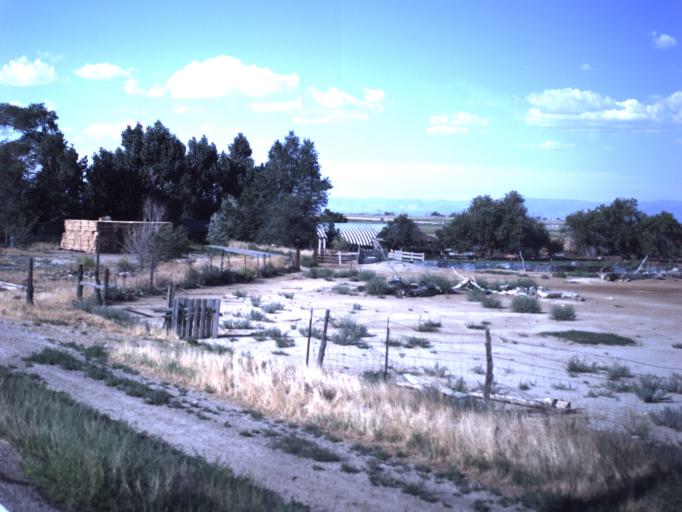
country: US
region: Utah
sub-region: Emery County
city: Huntington
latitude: 39.3739
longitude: -110.8523
